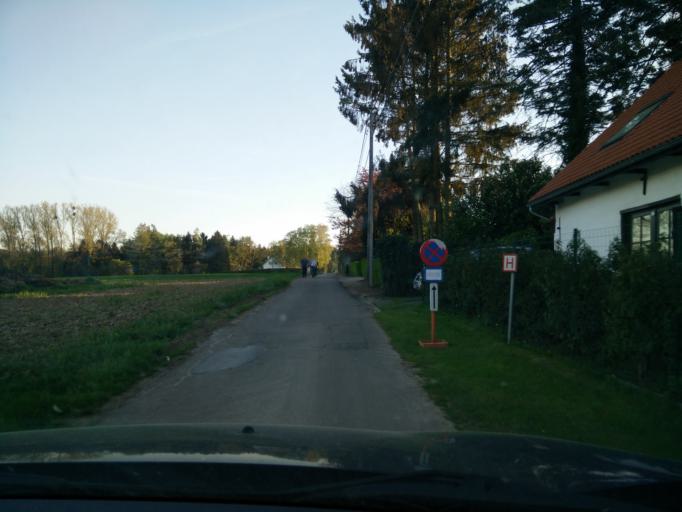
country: BE
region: Wallonia
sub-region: Province du Brabant Wallon
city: Braine-le-Chateau
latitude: 50.7185
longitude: 4.2853
